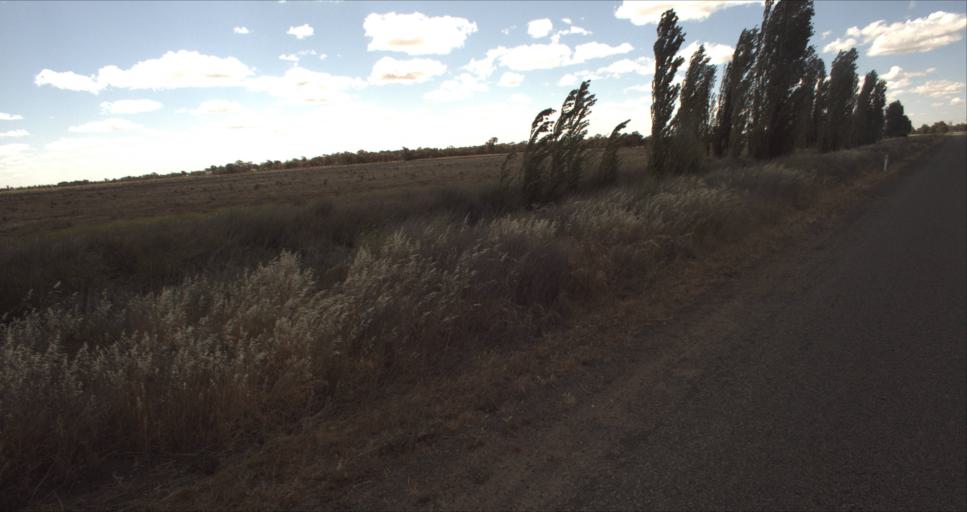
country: AU
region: New South Wales
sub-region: Leeton
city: Leeton
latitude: -34.5282
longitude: 146.2198
